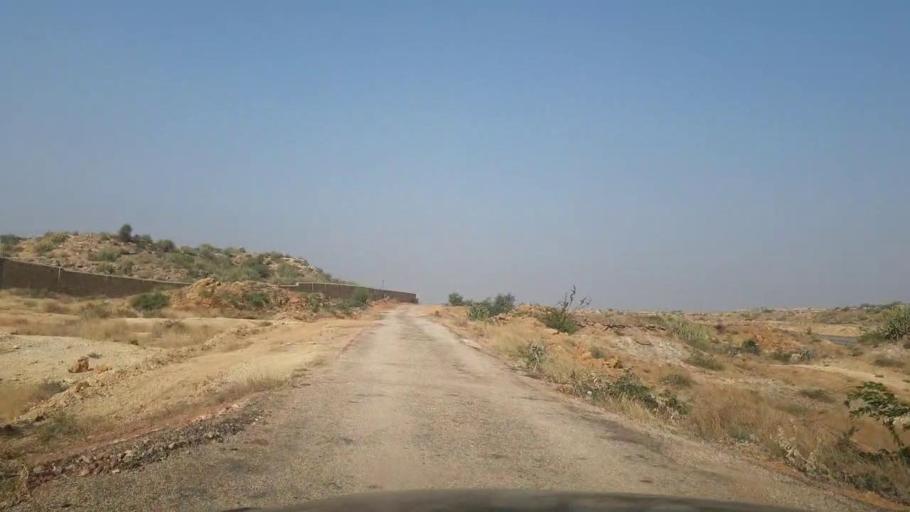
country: PK
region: Sindh
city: Gharo
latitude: 25.0493
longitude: 67.5447
